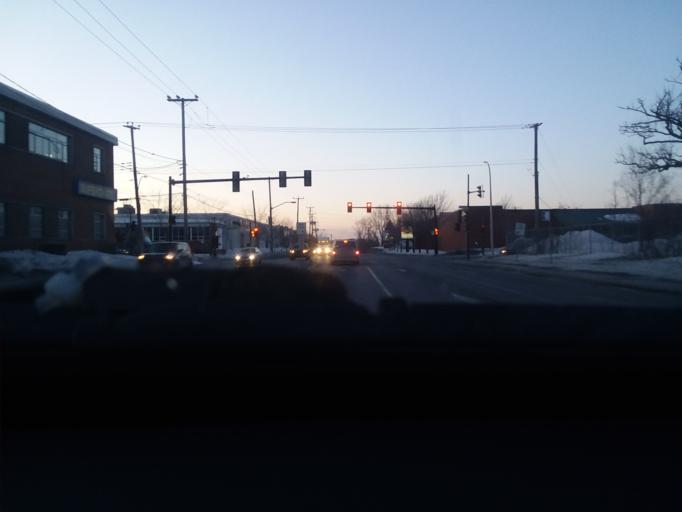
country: CA
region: Quebec
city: Montreal-Ouest
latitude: 45.4372
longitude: -73.6420
